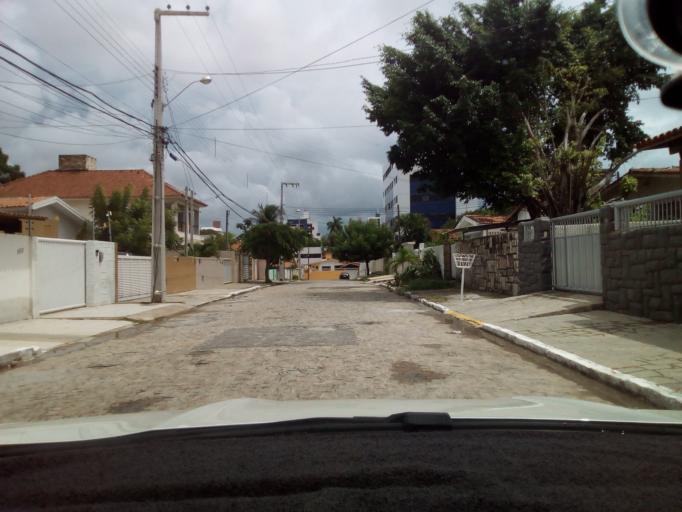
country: BR
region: Paraiba
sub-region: Joao Pessoa
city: Joao Pessoa
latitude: -7.1236
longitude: -34.8494
